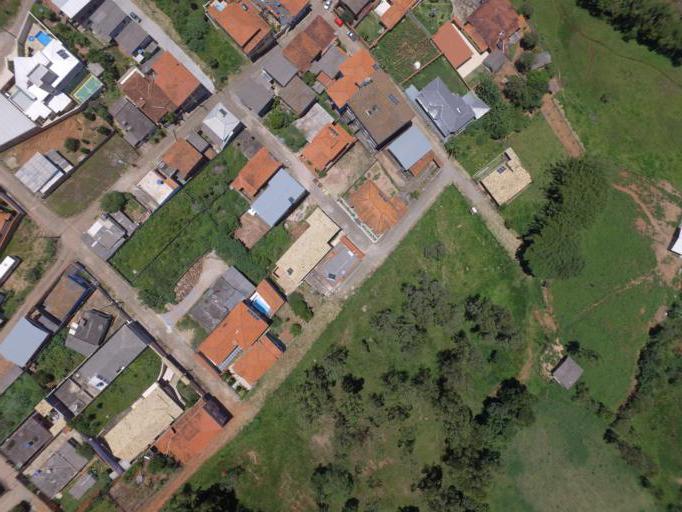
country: BR
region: Minas Gerais
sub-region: Tiradentes
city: Tiradentes
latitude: -21.0631
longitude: -44.0773
